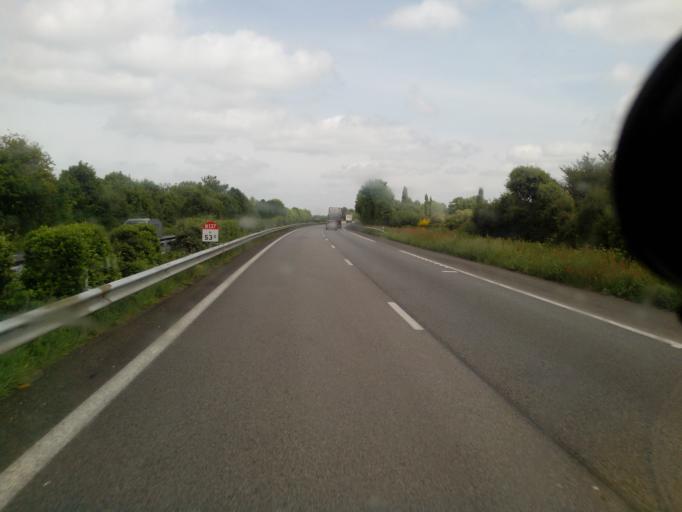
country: FR
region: Pays de la Loire
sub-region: Departement de la Loire-Atlantique
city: Heric
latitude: 47.4702
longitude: -1.6377
